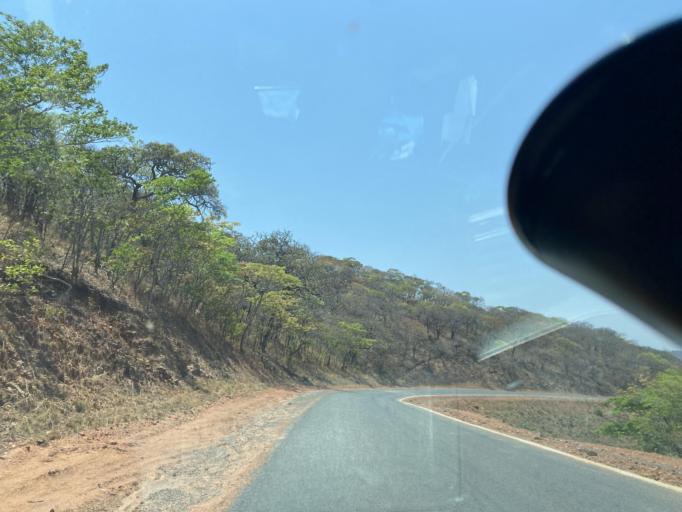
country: ZM
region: Lusaka
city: Kafue
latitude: -15.8585
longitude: 28.4209
